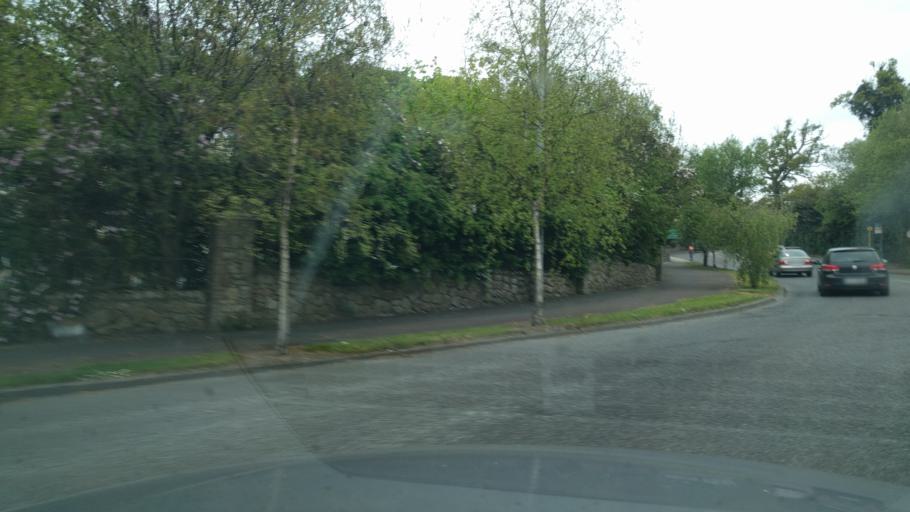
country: IE
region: Leinster
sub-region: Wicklow
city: Bray
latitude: 53.1878
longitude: -6.1001
